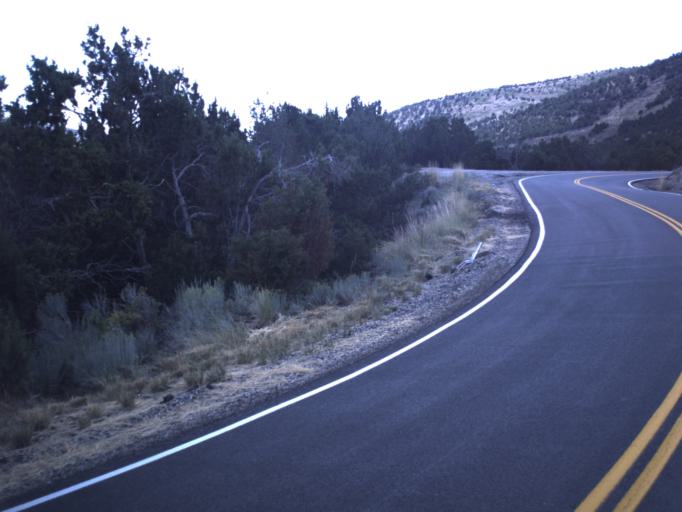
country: US
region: Utah
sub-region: Tooele County
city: Grantsville
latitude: 40.3375
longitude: -112.5690
